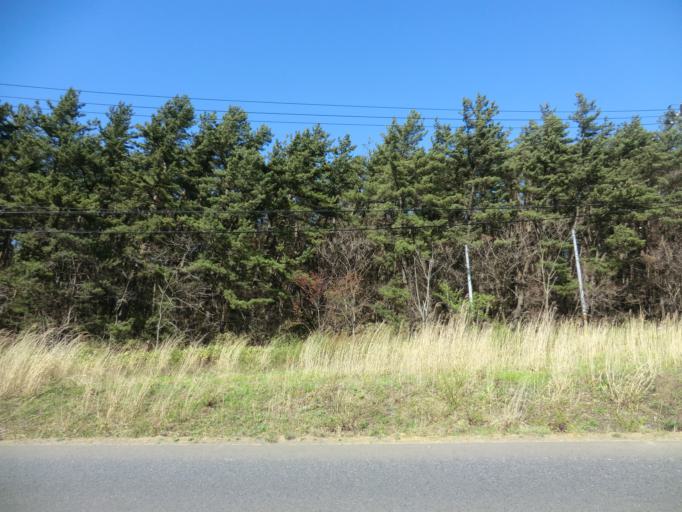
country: JP
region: Aomori
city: Misawa
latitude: 40.9267
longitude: 141.3789
